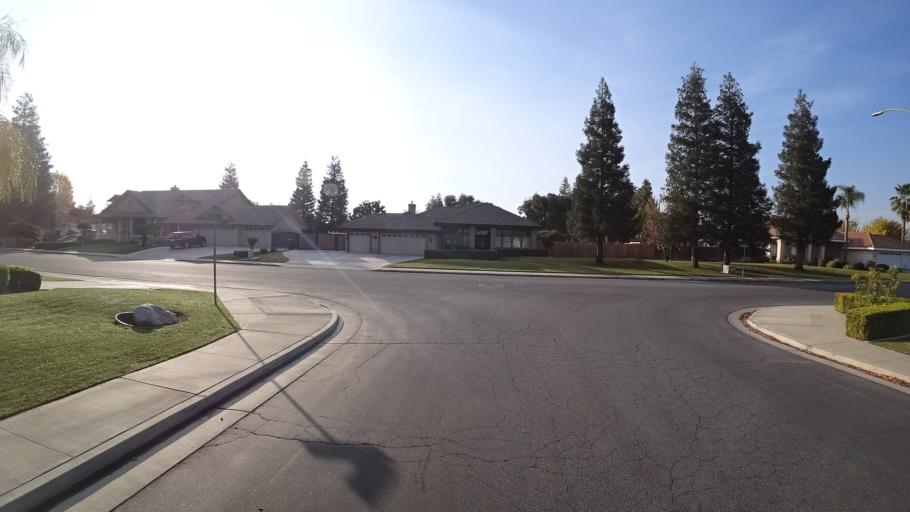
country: US
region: California
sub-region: Kern County
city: Greenacres
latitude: 35.3732
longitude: -119.1266
